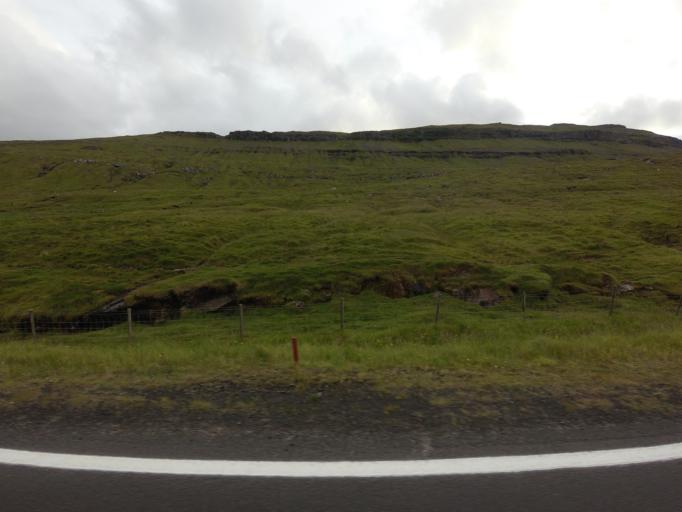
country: FO
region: Streymoy
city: Kollafjordhur
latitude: 62.1326
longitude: -6.8841
